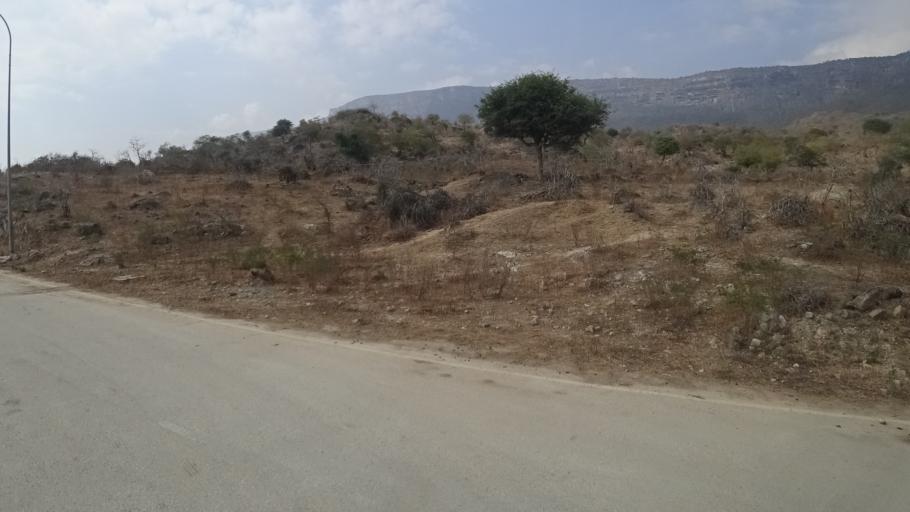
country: YE
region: Al Mahrah
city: Hawf
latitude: 16.7093
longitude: 53.2618
